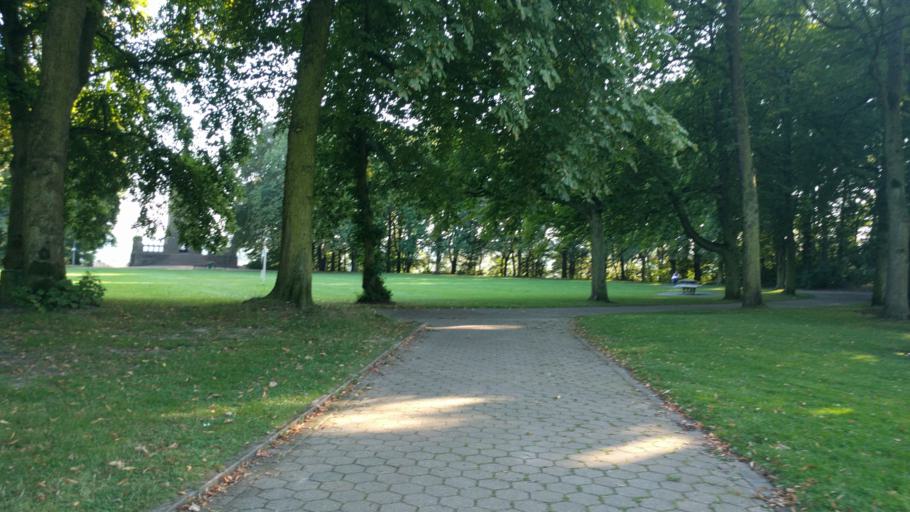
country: DE
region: North Rhine-Westphalia
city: Witten
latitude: 51.4270
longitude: 7.3521
